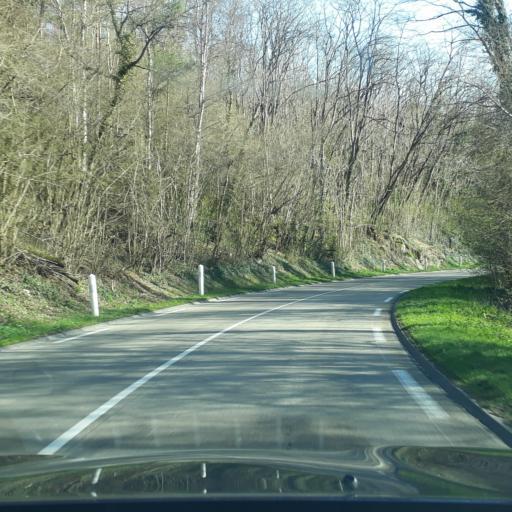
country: FR
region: Ile-de-France
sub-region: Departement de l'Essonne
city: Boissy-le-Cutte
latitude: 48.4627
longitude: 2.2688
